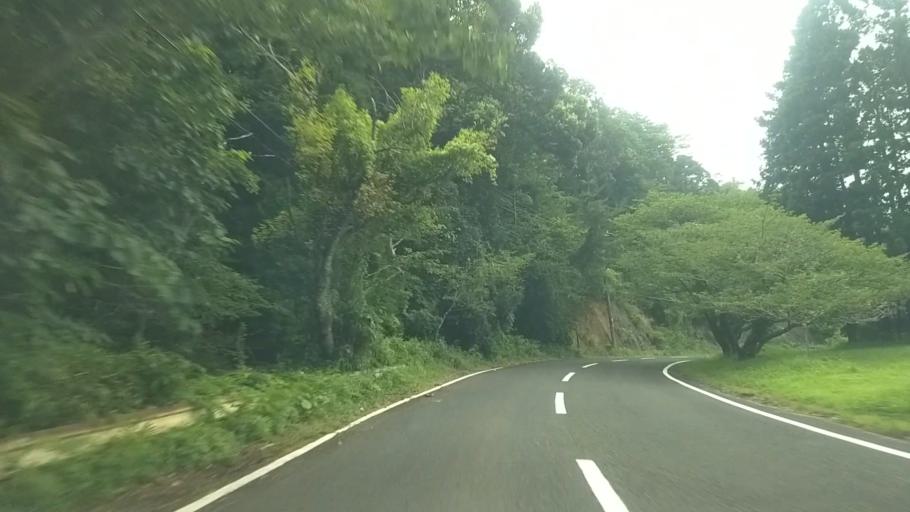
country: JP
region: Chiba
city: Kawaguchi
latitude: 35.1720
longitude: 140.1345
